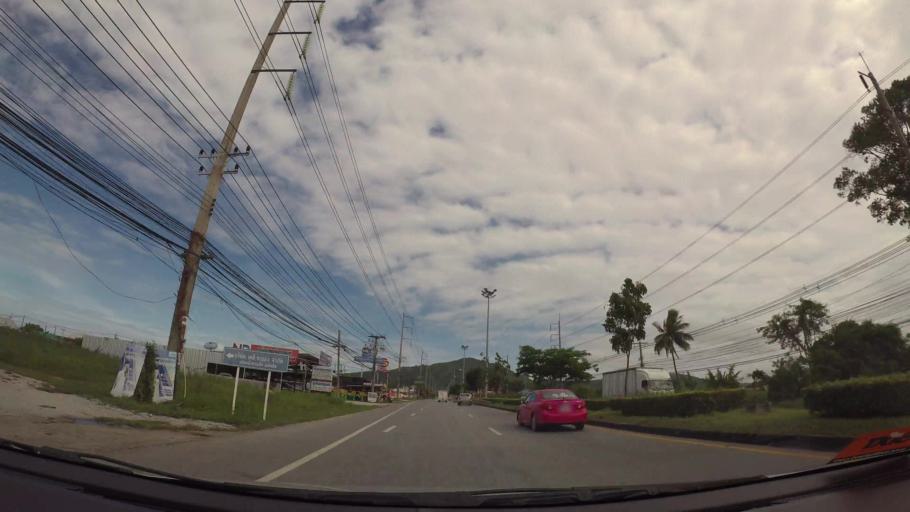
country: TH
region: Rayong
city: Ban Chang
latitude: 12.7444
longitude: 101.1150
